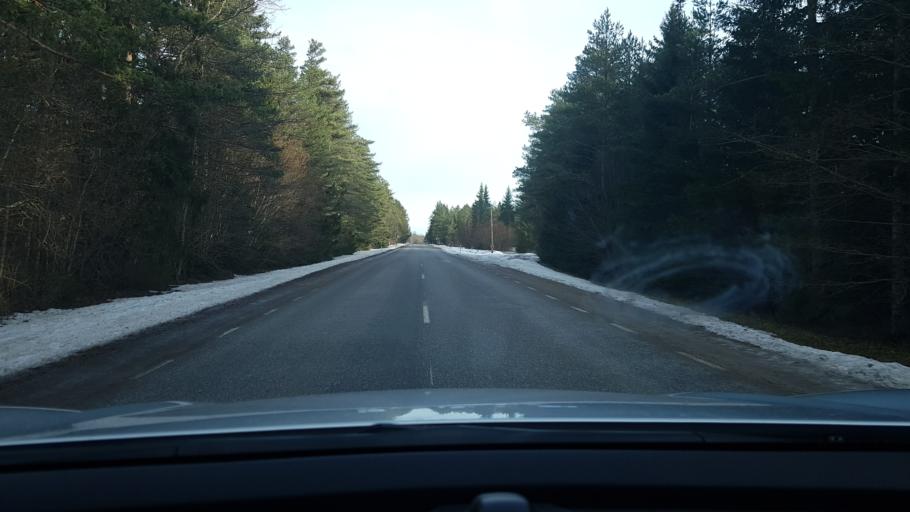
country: EE
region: Saare
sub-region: Kuressaare linn
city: Kuressaare
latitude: 58.4115
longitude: 22.6565
